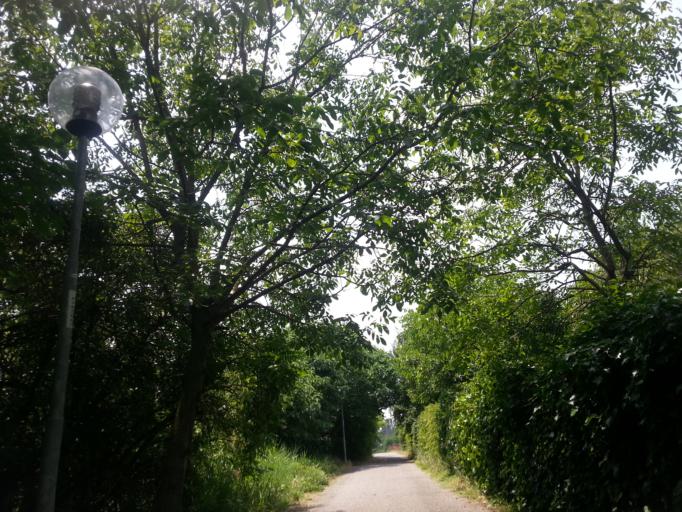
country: IT
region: Emilia-Romagna
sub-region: Provincia di Reggio Emilia
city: Reggio nell'Emilia
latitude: 44.6707
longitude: 10.6115
